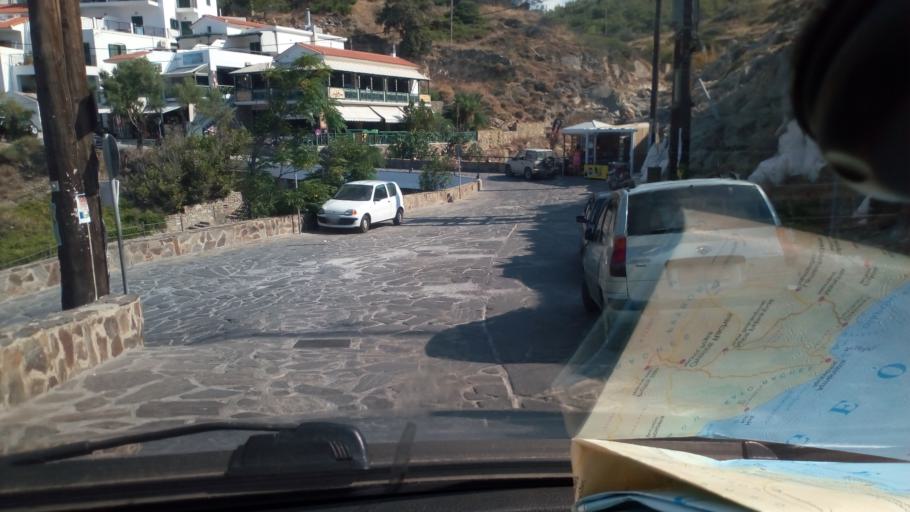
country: GR
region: North Aegean
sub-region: Nomos Samou
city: Agios Kirykos
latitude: 37.6334
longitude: 26.0879
